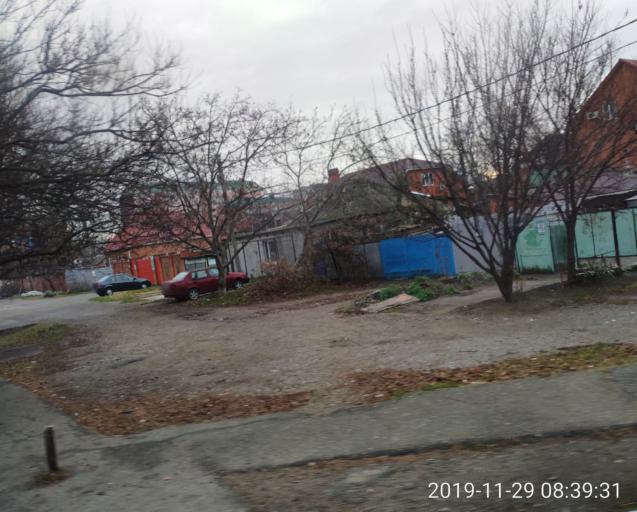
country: RU
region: Krasnodarskiy
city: Krasnodar
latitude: 45.0485
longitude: 38.9977
